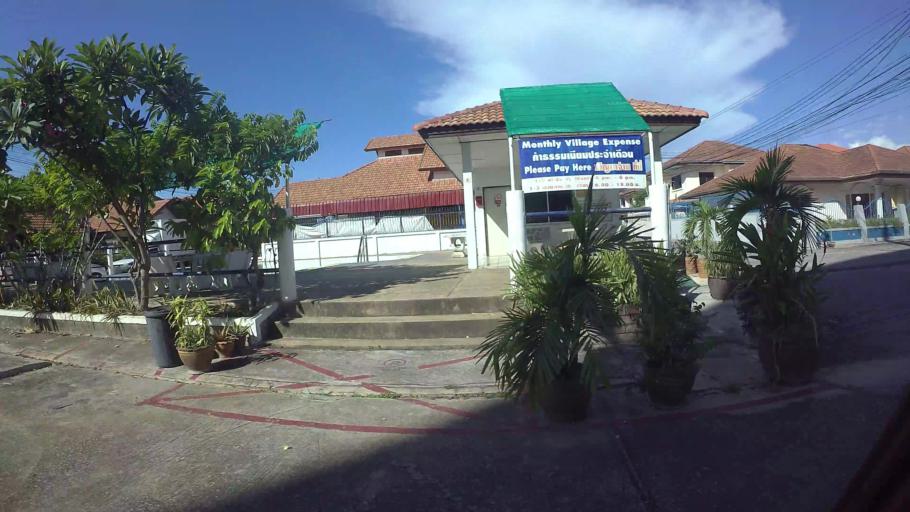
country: TH
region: Chon Buri
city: Phatthaya
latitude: 12.9049
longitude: 100.8778
